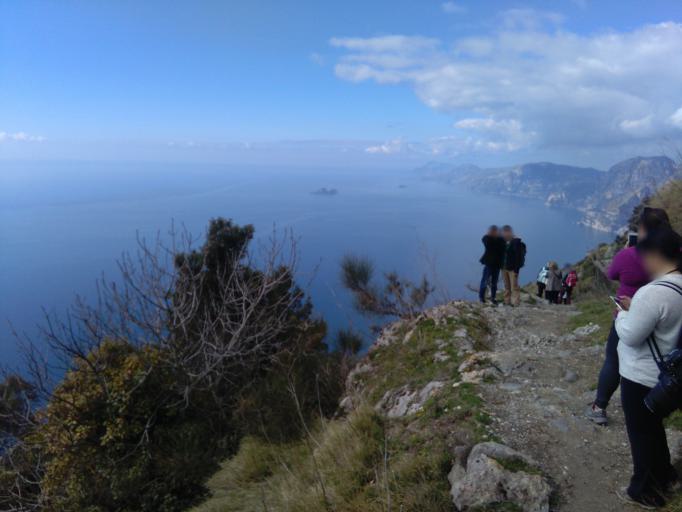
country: IT
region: Campania
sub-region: Provincia di Salerno
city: Praiano
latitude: 40.6208
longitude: 14.5260
